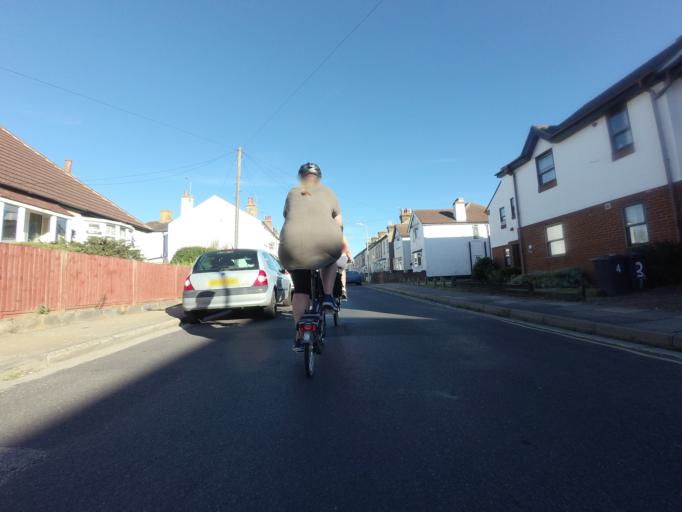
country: GB
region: England
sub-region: Kent
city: Herne Bay
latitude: 51.3652
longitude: 1.1121
